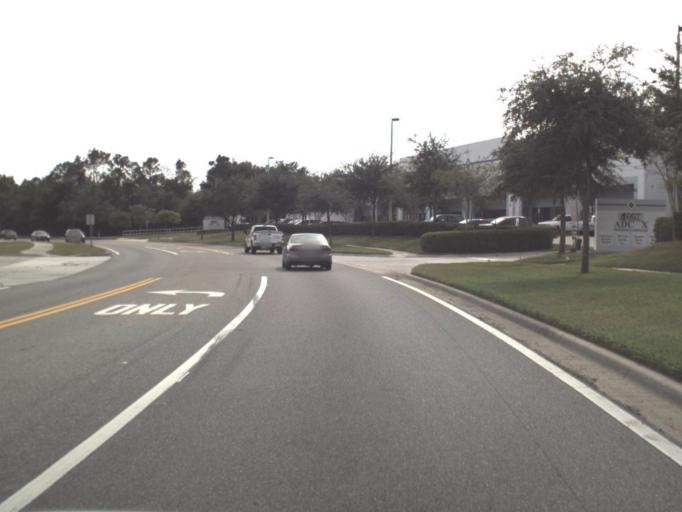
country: US
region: Florida
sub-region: Orange County
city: Belle Isle
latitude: 28.4467
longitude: -81.3500
